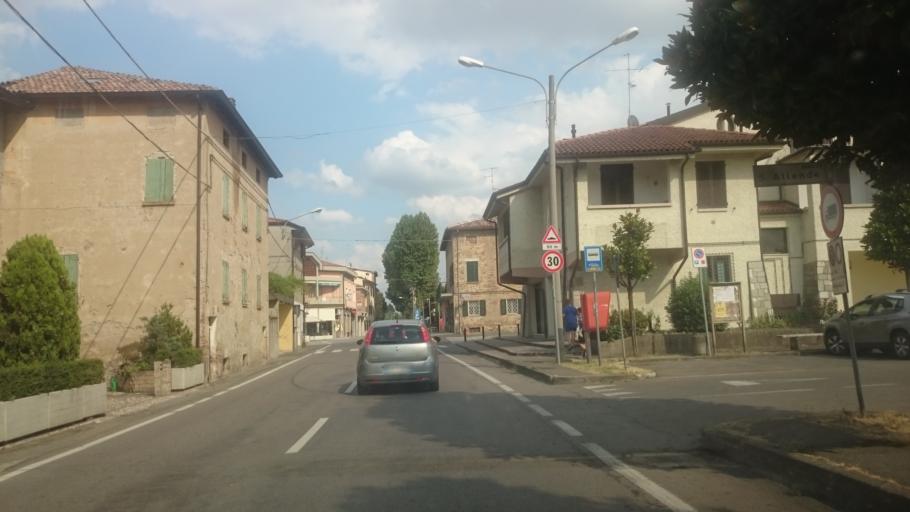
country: IT
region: Emilia-Romagna
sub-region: Provincia di Reggio Emilia
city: Salvaterra
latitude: 44.6013
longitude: 10.7665
